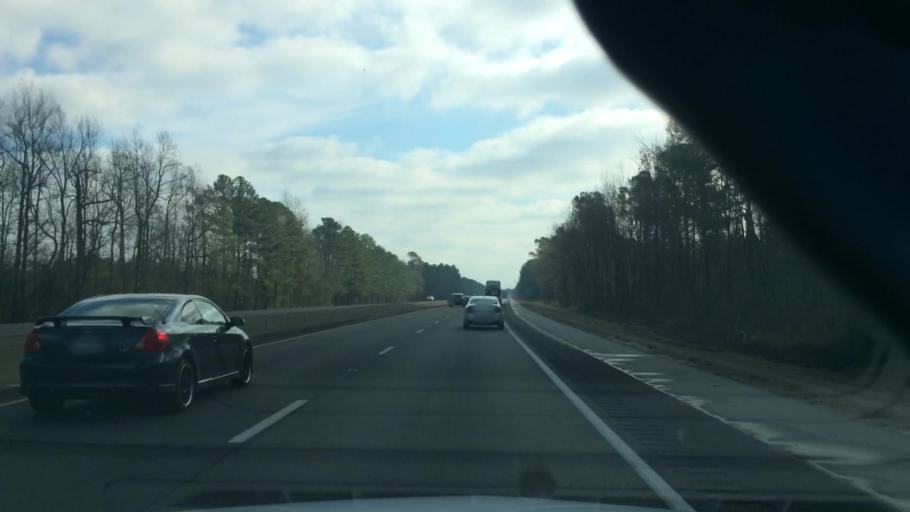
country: US
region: North Carolina
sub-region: Pender County
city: Burgaw
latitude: 34.6071
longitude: -77.9167
